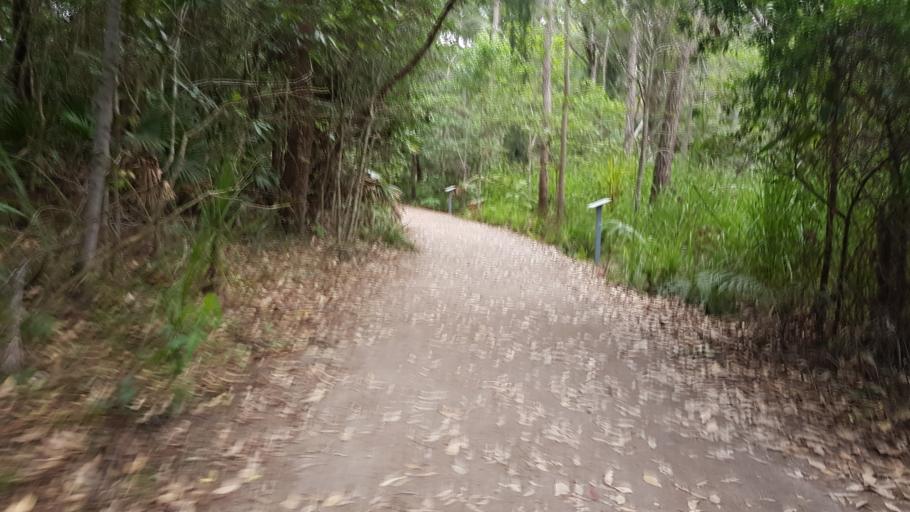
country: AU
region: New South Wales
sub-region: Warringah
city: Narrabeen
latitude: -33.7201
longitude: 151.2781
